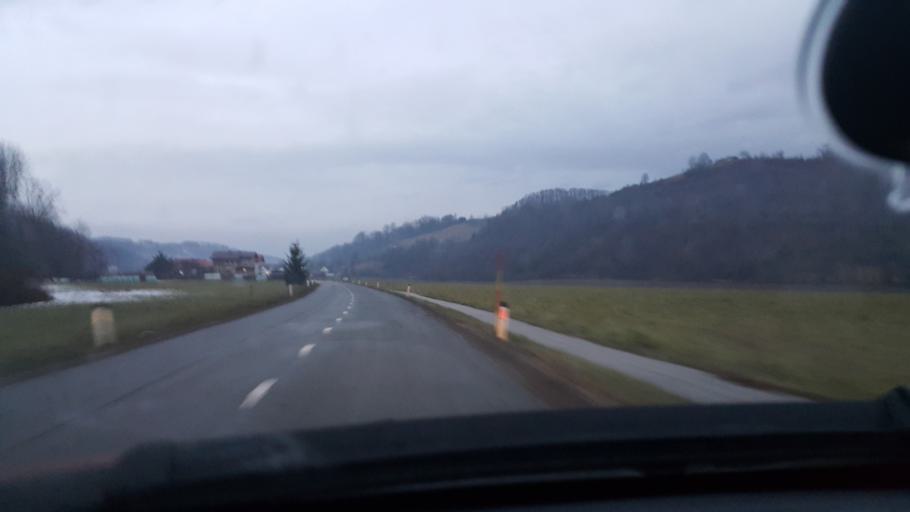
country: SI
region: Kungota
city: Zgornja Kungota
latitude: 46.6252
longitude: 15.6320
